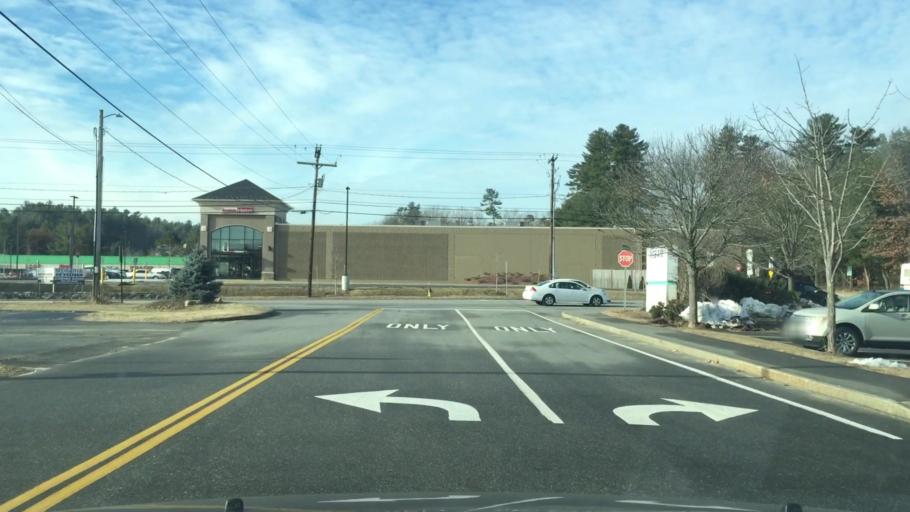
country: US
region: New Hampshire
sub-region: Hillsborough County
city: Pinardville
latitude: 42.9652
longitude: -71.4805
